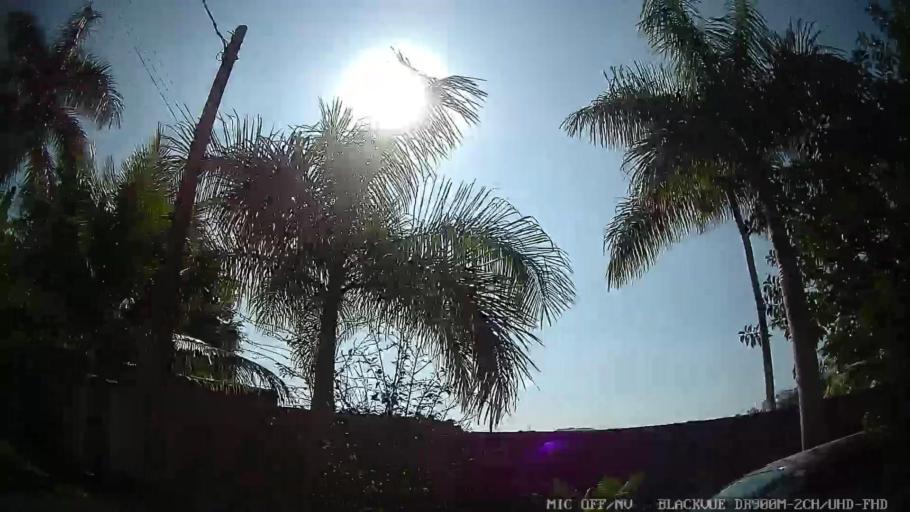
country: BR
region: Sao Paulo
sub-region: Guaruja
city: Guaruja
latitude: -24.0087
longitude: -46.2774
